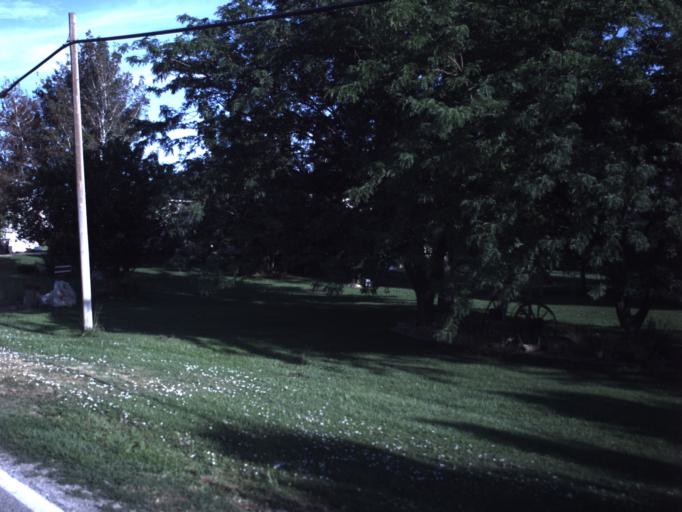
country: US
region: Utah
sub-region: Weber County
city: Plain City
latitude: 41.3052
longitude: -112.0687
